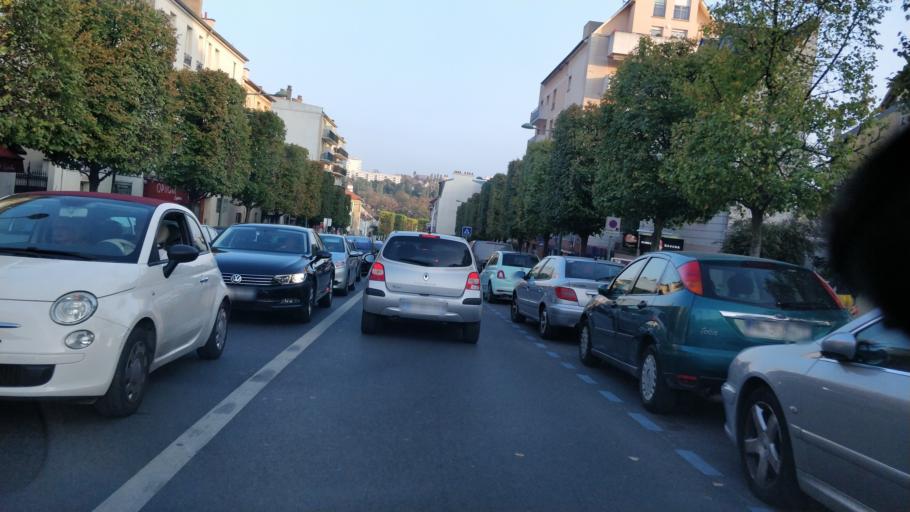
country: FR
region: Ile-de-France
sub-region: Departement du Val-de-Marne
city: Arcueil
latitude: 48.8076
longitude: 2.3343
